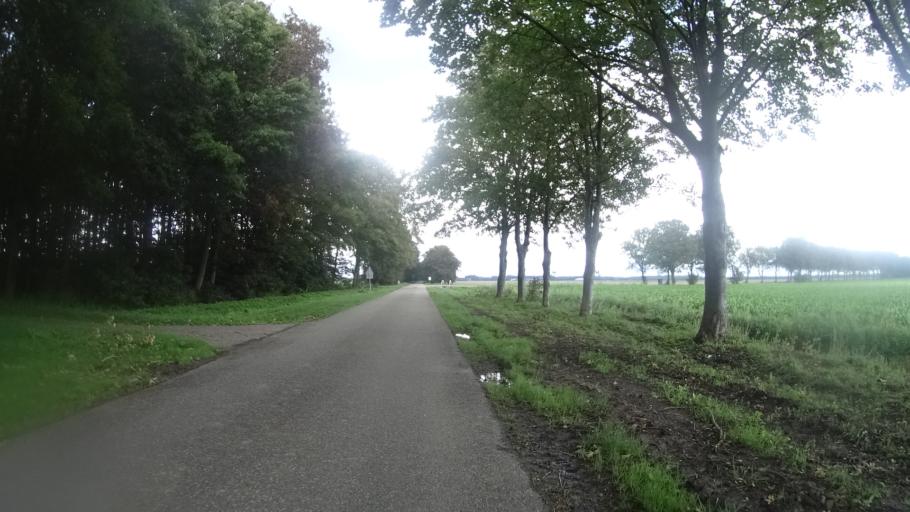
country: NL
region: North Holland
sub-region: Gemeente Hollands Kroon
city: Den Oever
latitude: 52.8920
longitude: 4.9773
